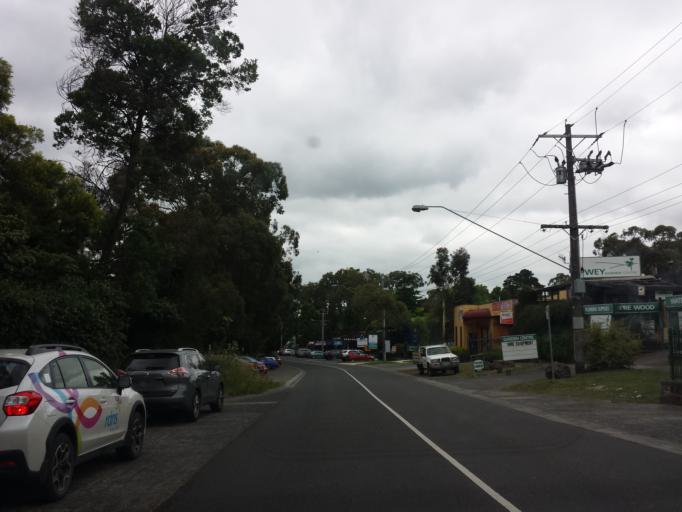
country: AU
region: Victoria
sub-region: Yarra Ranges
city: Tremont
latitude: -37.9042
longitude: 145.3318
